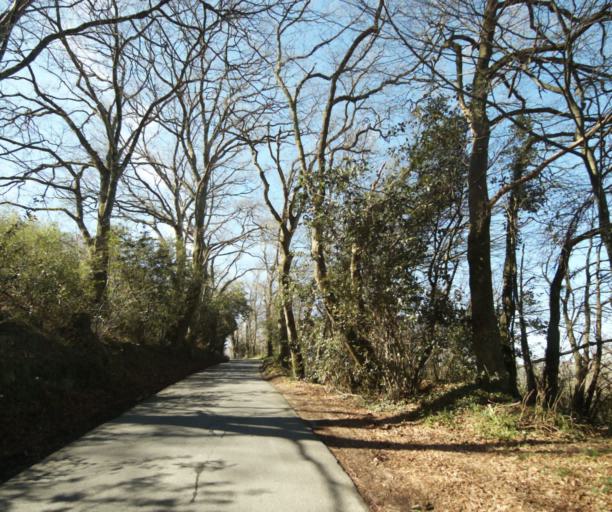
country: FR
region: Aquitaine
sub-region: Departement des Pyrenees-Atlantiques
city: Ciboure
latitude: 43.3680
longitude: -1.6755
